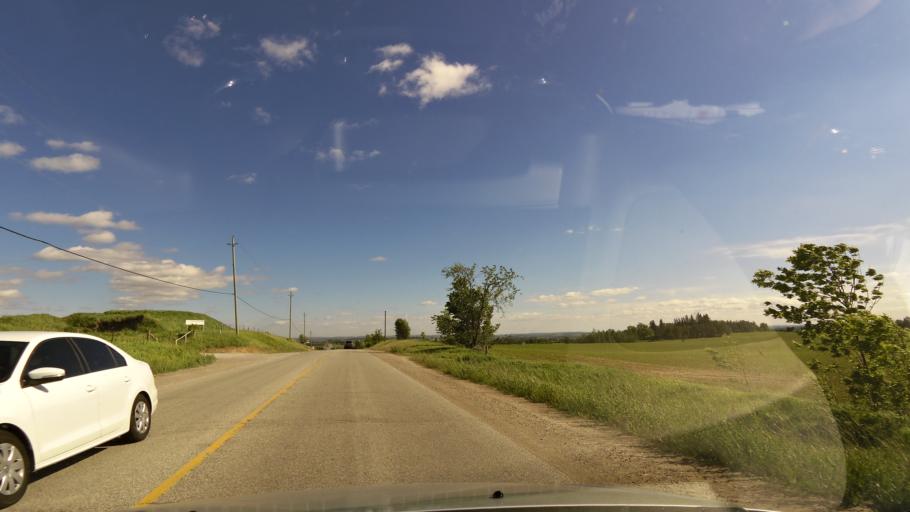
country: CA
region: Ontario
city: Bradford West Gwillimbury
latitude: 44.1229
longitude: -79.6063
